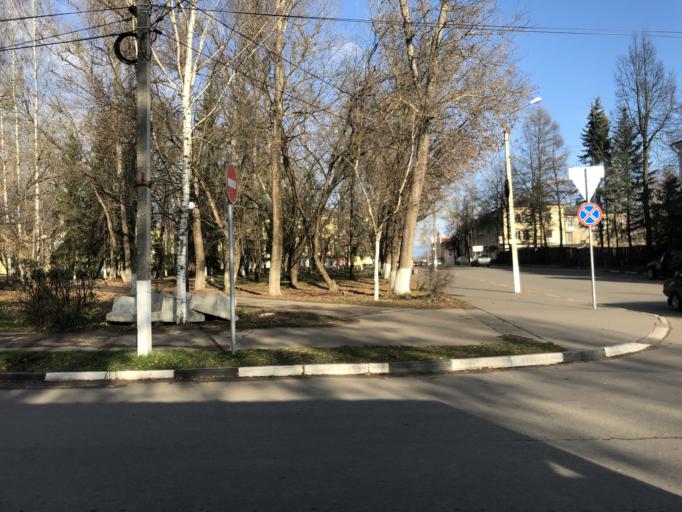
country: RU
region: Tverskaya
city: Rzhev
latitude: 56.2626
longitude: 34.3370
